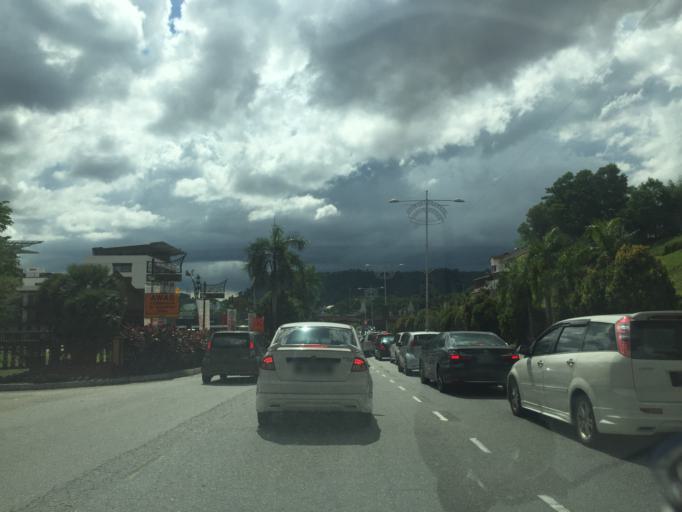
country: MY
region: Negeri Sembilan
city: Seremban
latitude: 2.7185
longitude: 101.9204
